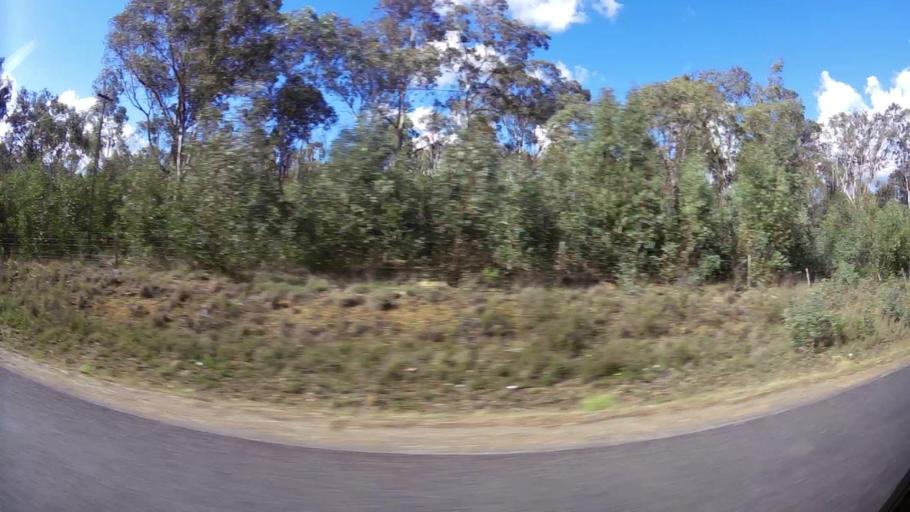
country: ZA
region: Western Cape
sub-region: Overberg District Municipality
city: Swellendam
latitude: -34.0291
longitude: 20.4206
